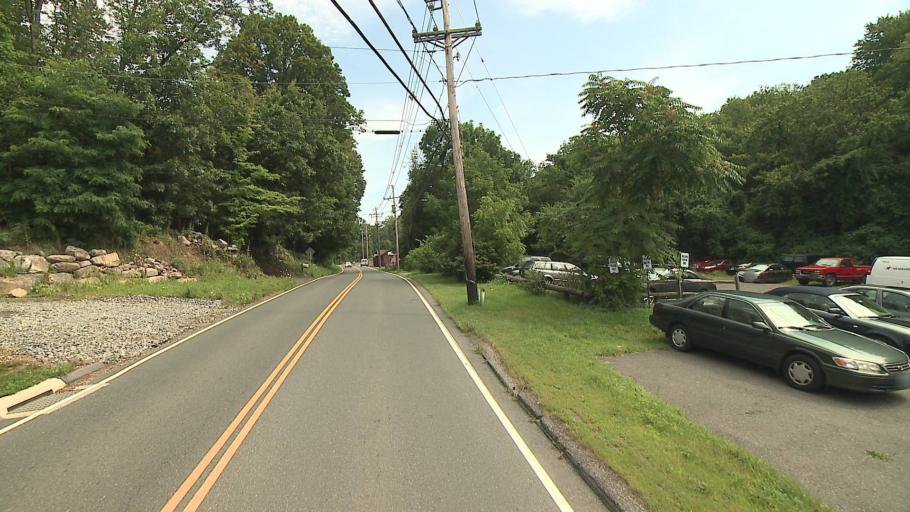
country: US
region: New York
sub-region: Putnam County
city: Putnam Lake
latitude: 41.4703
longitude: -73.4713
